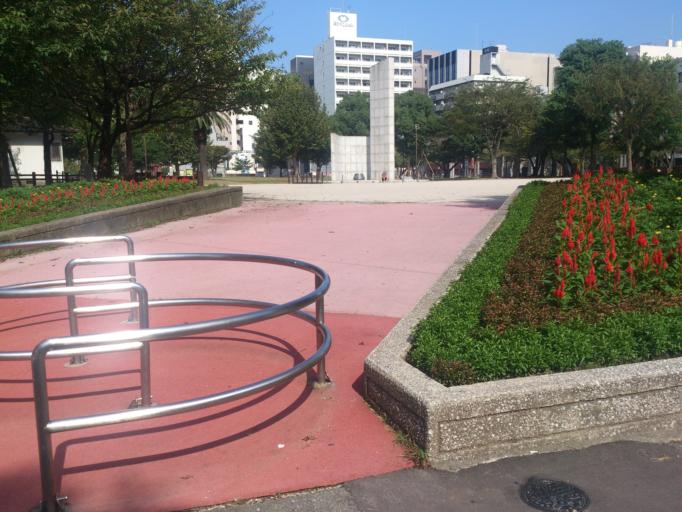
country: JP
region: Fukuoka
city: Fukuoka-shi
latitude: 33.5938
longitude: 130.4091
